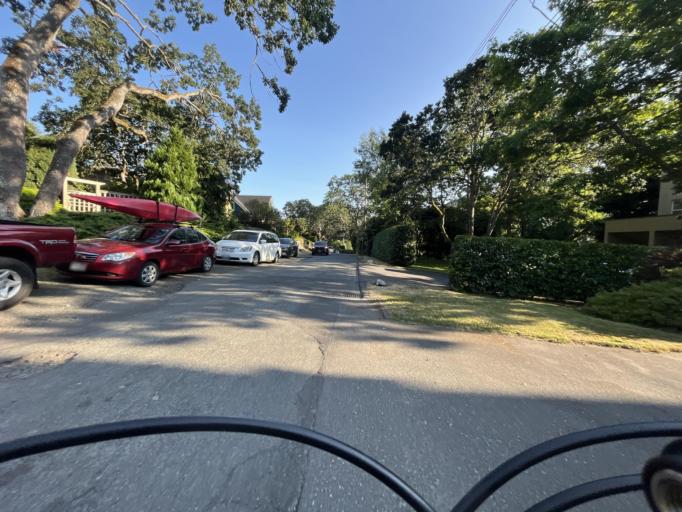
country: CA
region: British Columbia
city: Victoria
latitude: 48.4207
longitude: -123.3446
